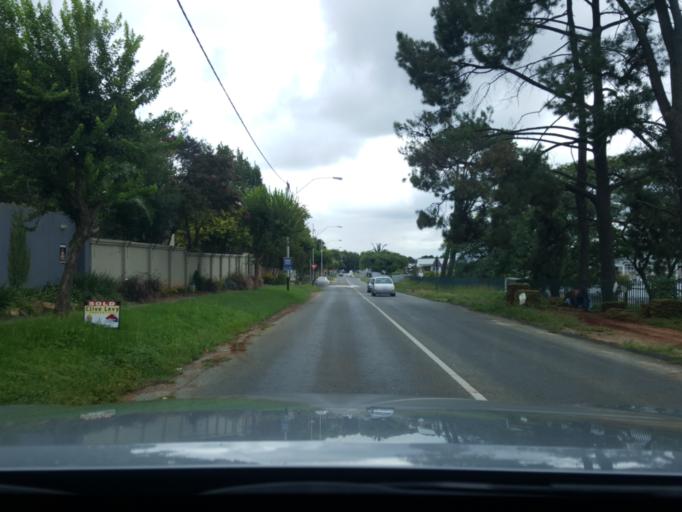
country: ZA
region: Gauteng
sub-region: City of Johannesburg Metropolitan Municipality
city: Johannesburg
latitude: -26.1242
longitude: 28.0032
